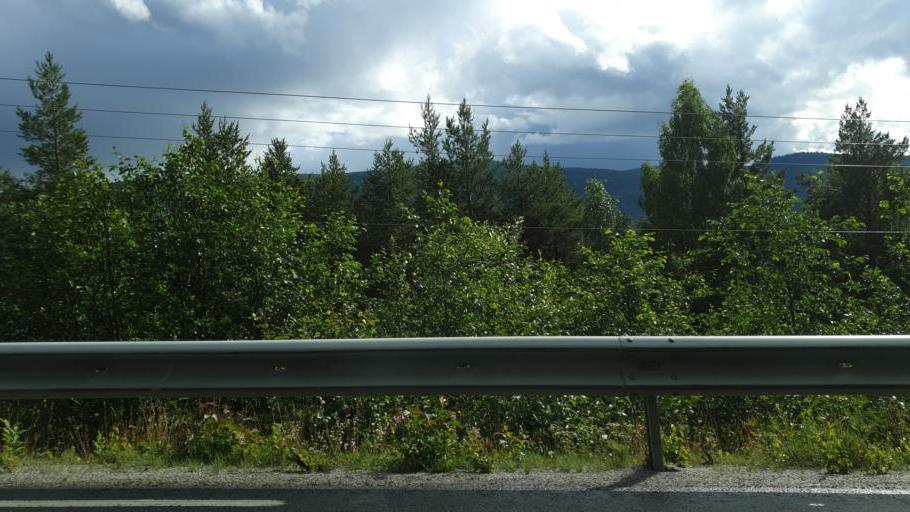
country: NO
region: Oppland
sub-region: Dovre
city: Dovre
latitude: 61.8686
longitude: 9.2227
